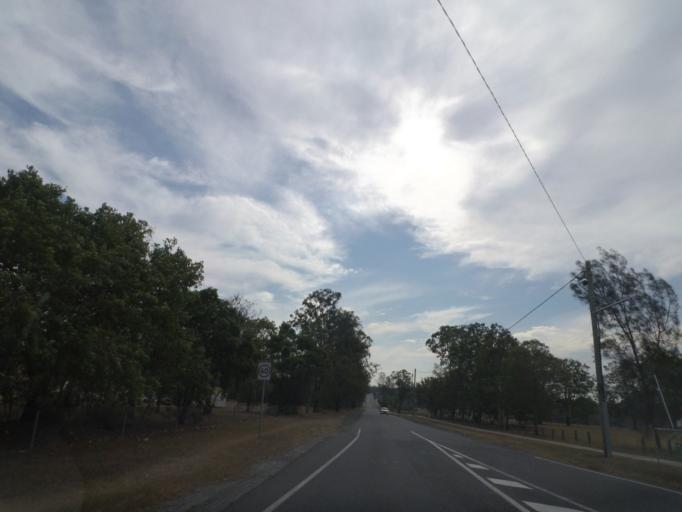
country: AU
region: Queensland
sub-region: Brisbane
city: Richlands
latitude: -27.5929
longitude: 152.9549
